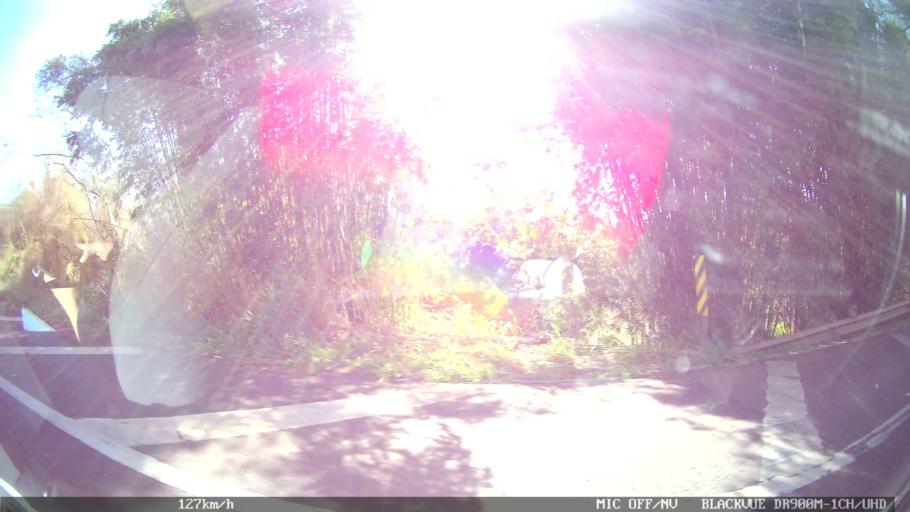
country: BR
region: Sao Paulo
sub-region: Barretos
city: Barretos
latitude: -20.5482
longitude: -48.6290
